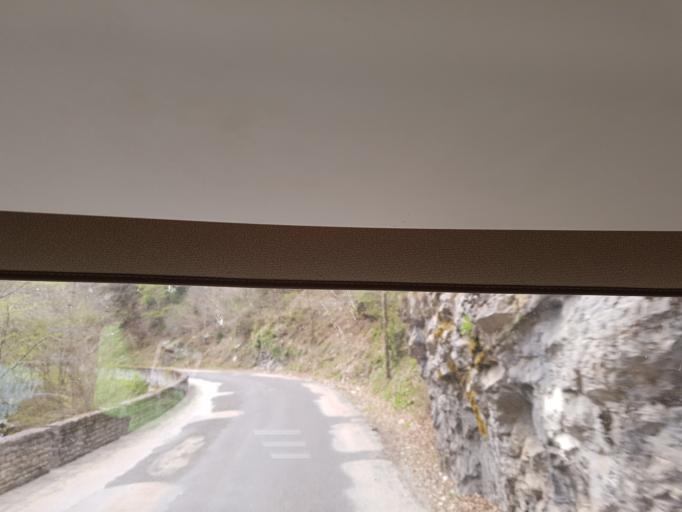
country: FR
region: Languedoc-Roussillon
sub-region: Departement de l'Aude
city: Quillan
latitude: 42.7679
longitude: 2.1047
